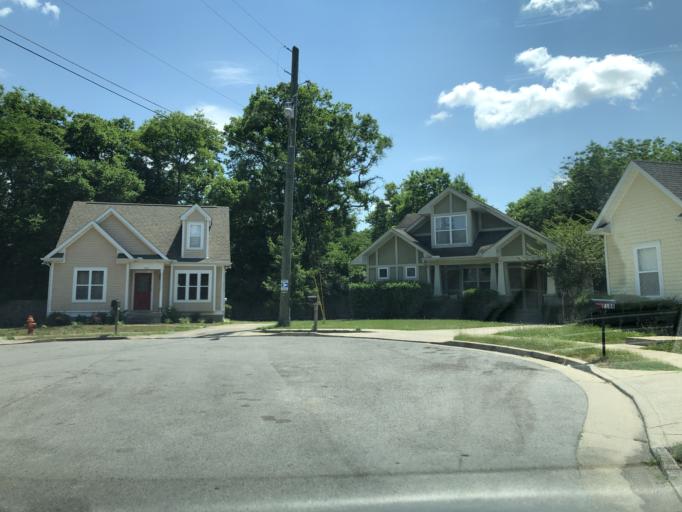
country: US
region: Tennessee
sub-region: Davidson County
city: Goodlettsville
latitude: 36.2615
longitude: -86.6975
